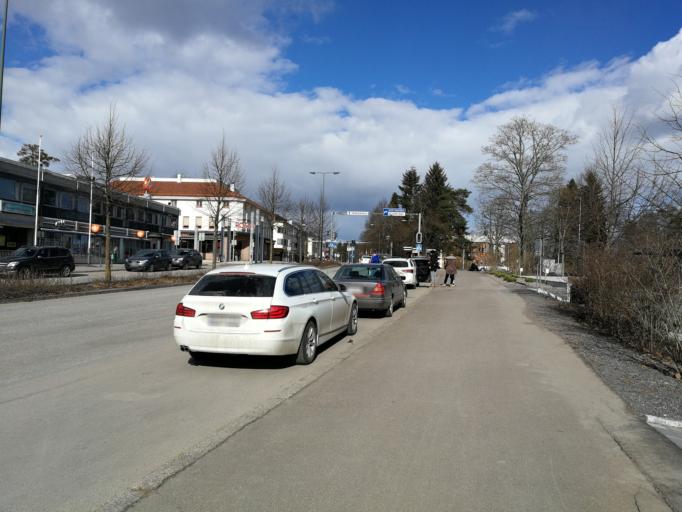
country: FI
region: South Karelia
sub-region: Imatra
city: Imatra
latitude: 61.1699
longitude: 28.7712
